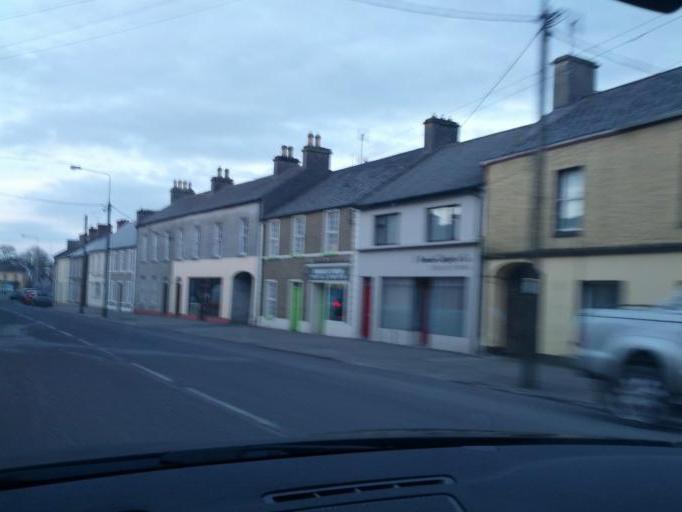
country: IE
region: Connaught
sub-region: County Galway
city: Portumna
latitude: 52.9960
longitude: -8.1274
